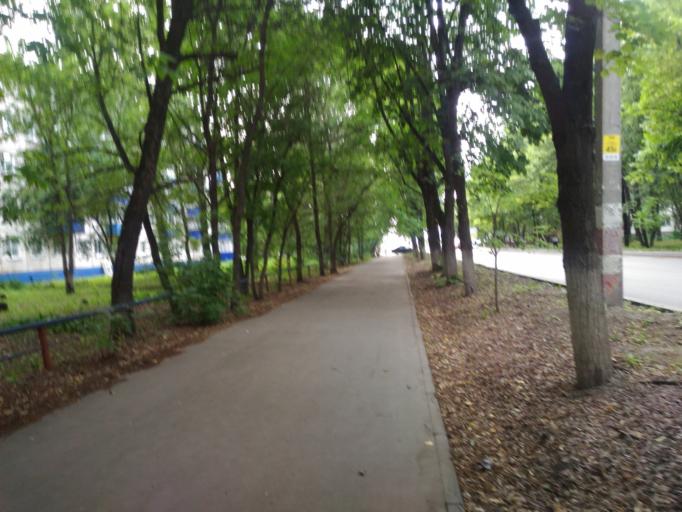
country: RU
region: Ulyanovsk
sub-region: Ulyanovskiy Rayon
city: Ulyanovsk
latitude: 54.2844
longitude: 48.2864
